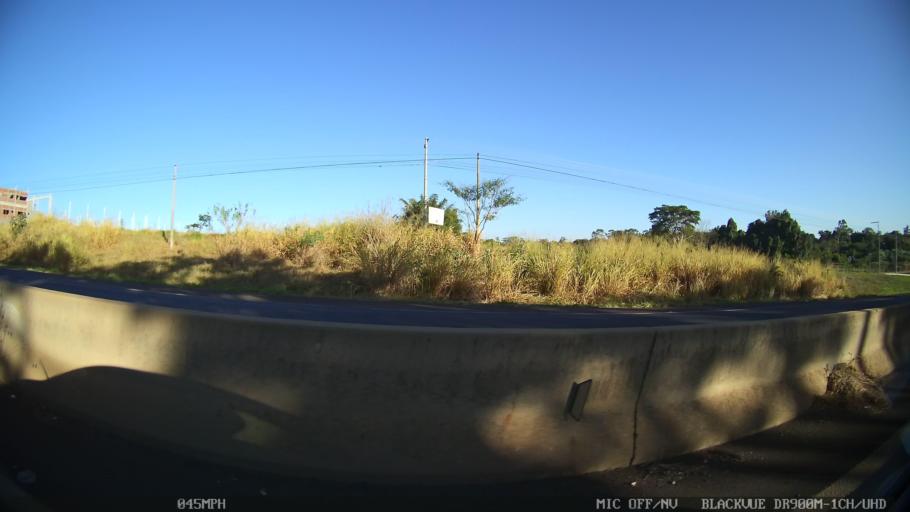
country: BR
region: Sao Paulo
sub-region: Guapiacu
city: Guapiacu
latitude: -20.7838
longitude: -49.2691
